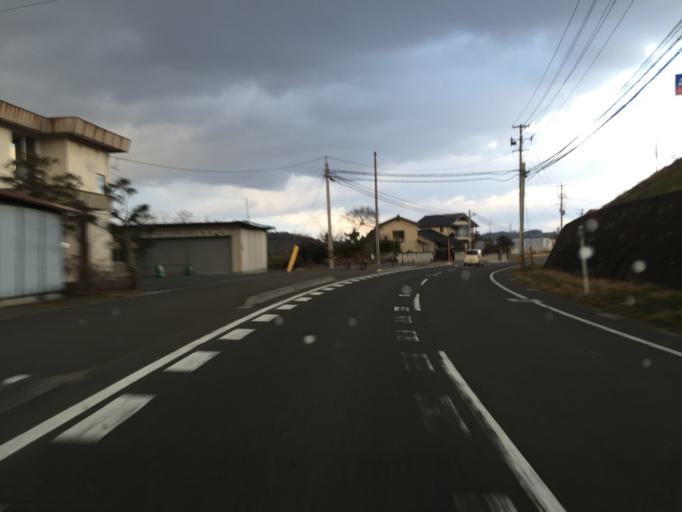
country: JP
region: Fukushima
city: Nihommatsu
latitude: 37.5856
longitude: 140.4561
